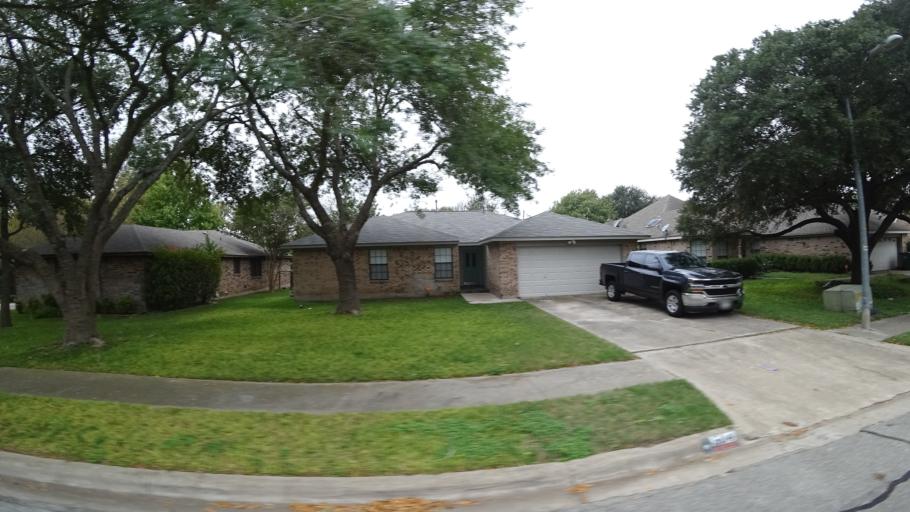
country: US
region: Texas
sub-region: Travis County
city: Pflugerville
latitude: 30.4423
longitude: -97.6164
